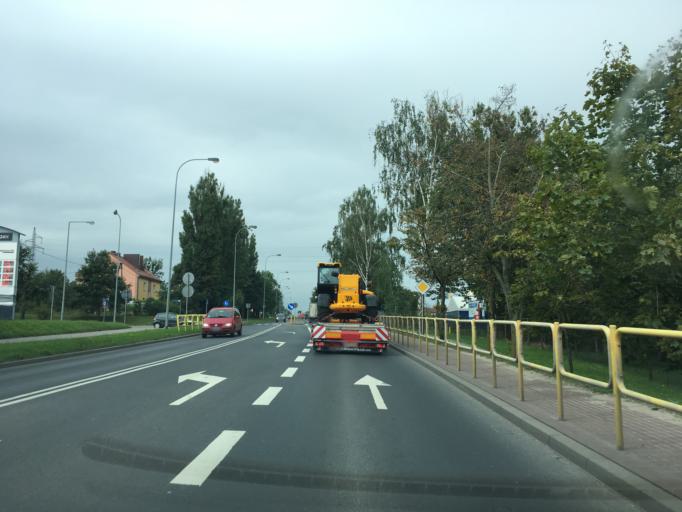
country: PL
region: Warmian-Masurian Voivodeship
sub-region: Powiat ostrodzki
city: Ostroda
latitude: 53.6894
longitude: 19.9839
